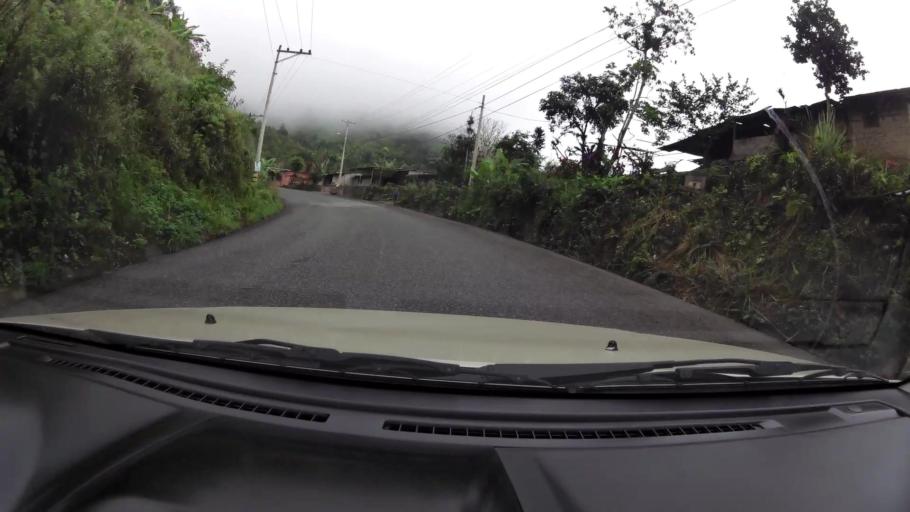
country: EC
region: El Oro
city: Pasaje
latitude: -3.3093
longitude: -79.5665
